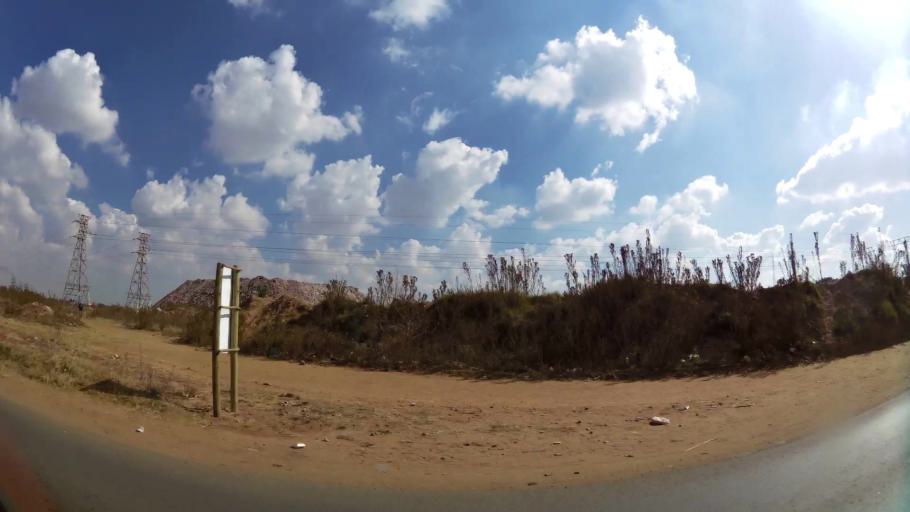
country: ZA
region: Gauteng
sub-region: City of Johannesburg Metropolitan Municipality
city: Roodepoort
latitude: -26.1856
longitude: 27.8686
